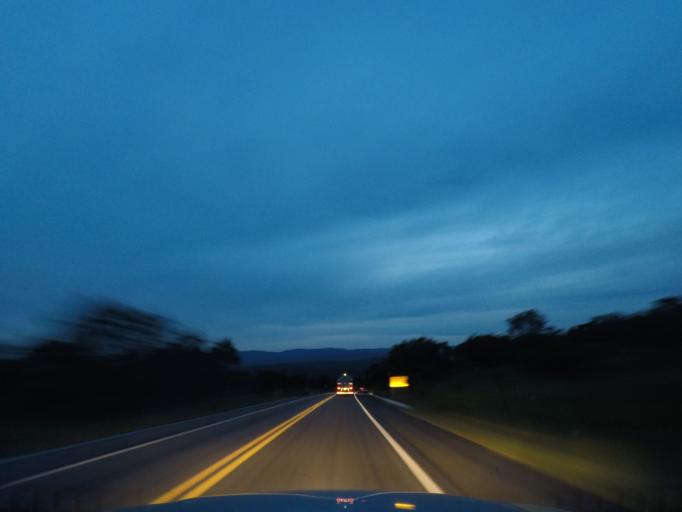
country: BR
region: Bahia
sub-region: Andarai
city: Vera Cruz
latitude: -12.4955
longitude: -41.3183
